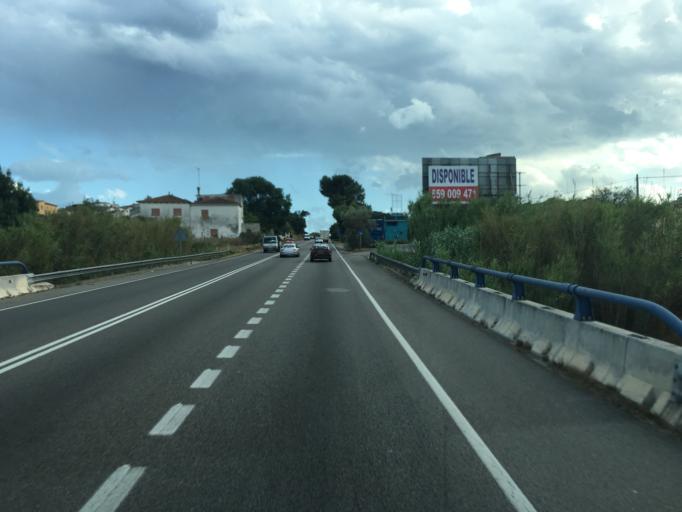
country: ES
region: Catalonia
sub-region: Provincia de Barcelona
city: Tordera
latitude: 41.6913
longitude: 2.7228
